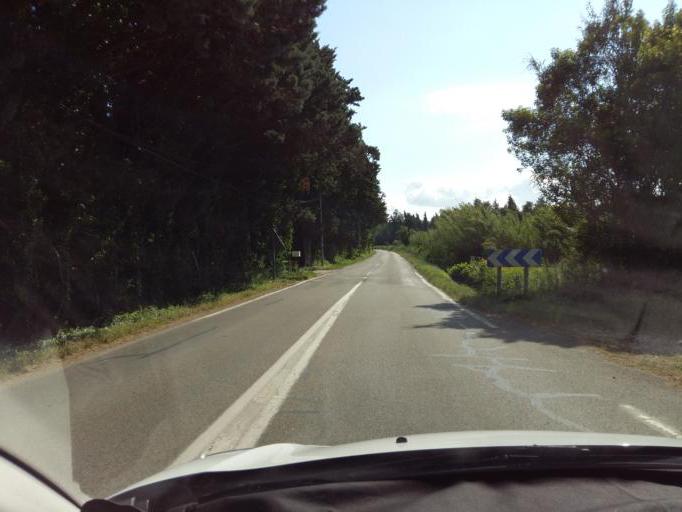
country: FR
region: Provence-Alpes-Cote d'Azur
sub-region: Departement du Vaucluse
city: Cavaillon
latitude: 43.8593
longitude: 5.0575
